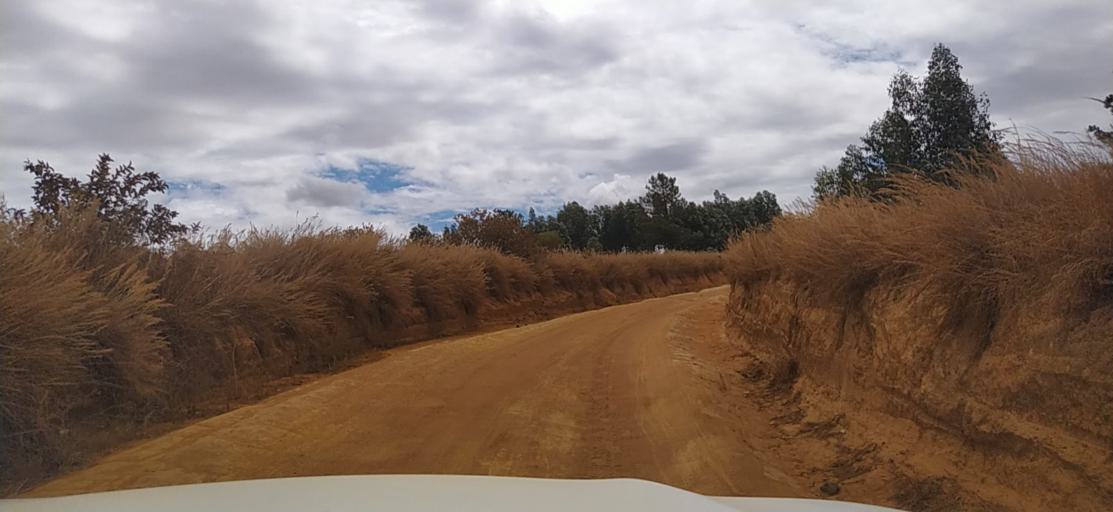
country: MG
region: Alaotra Mangoro
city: Ambatondrazaka
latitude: -17.9960
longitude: 48.2669
